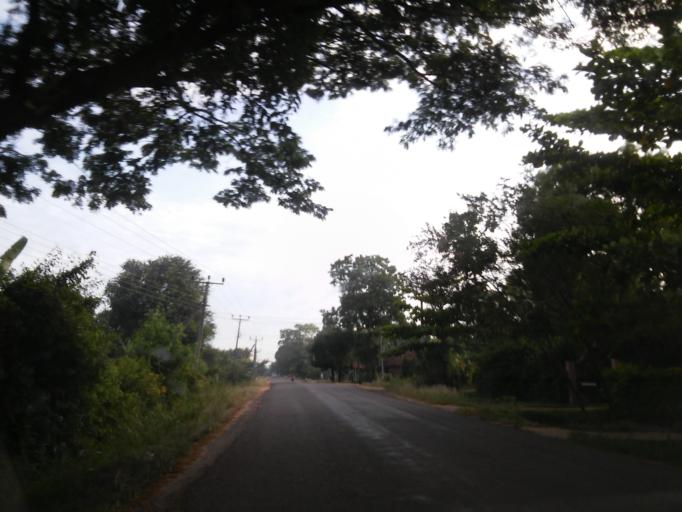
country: LK
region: Central
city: Sigiriya
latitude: 8.1225
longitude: 80.6329
